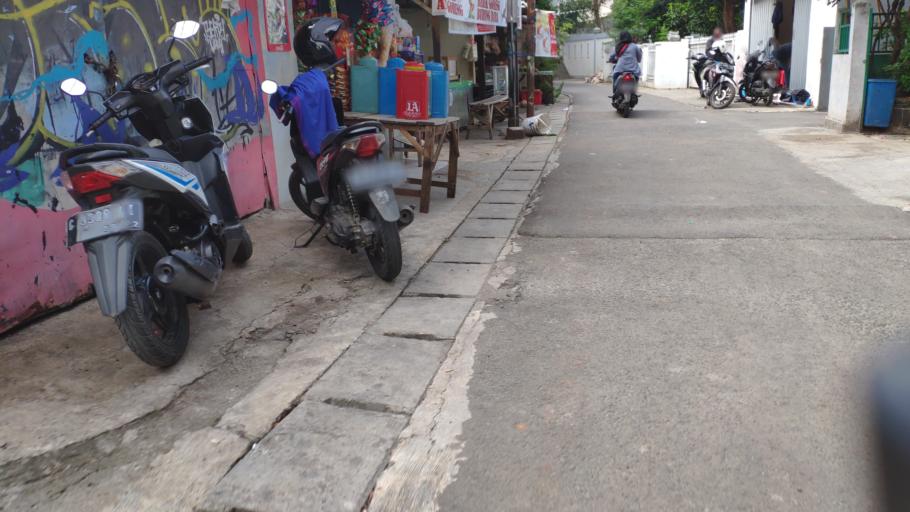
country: ID
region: West Java
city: Depok
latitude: -6.3196
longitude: 106.8261
